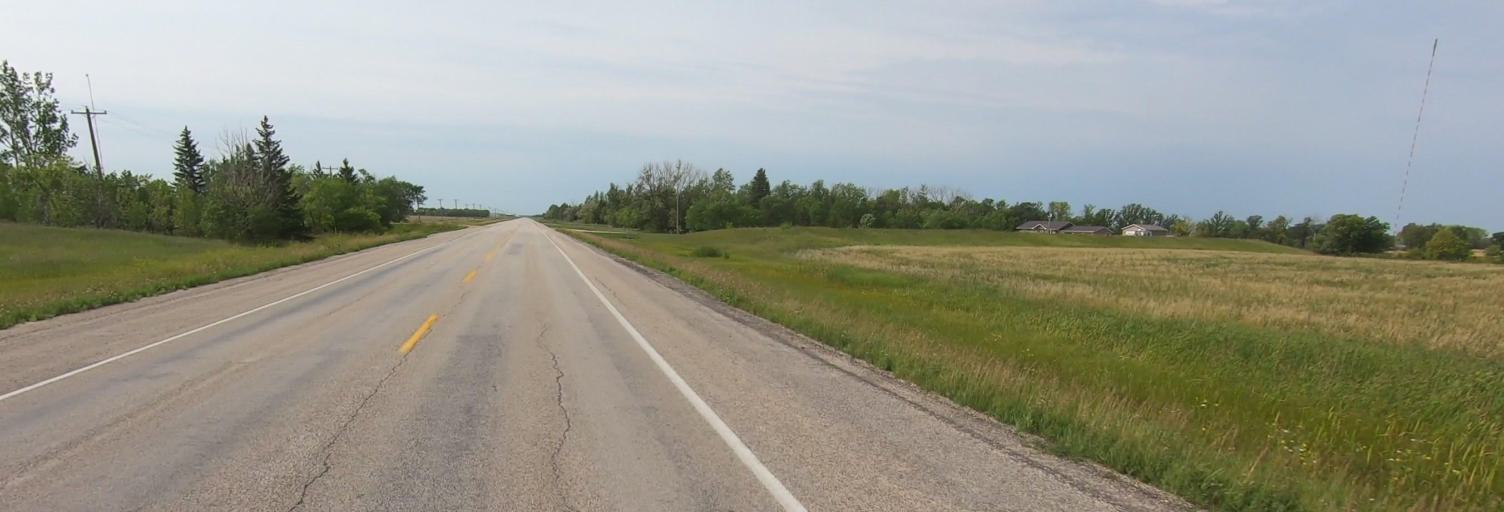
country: CA
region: Manitoba
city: Niverville
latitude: 49.5793
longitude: -97.1468
